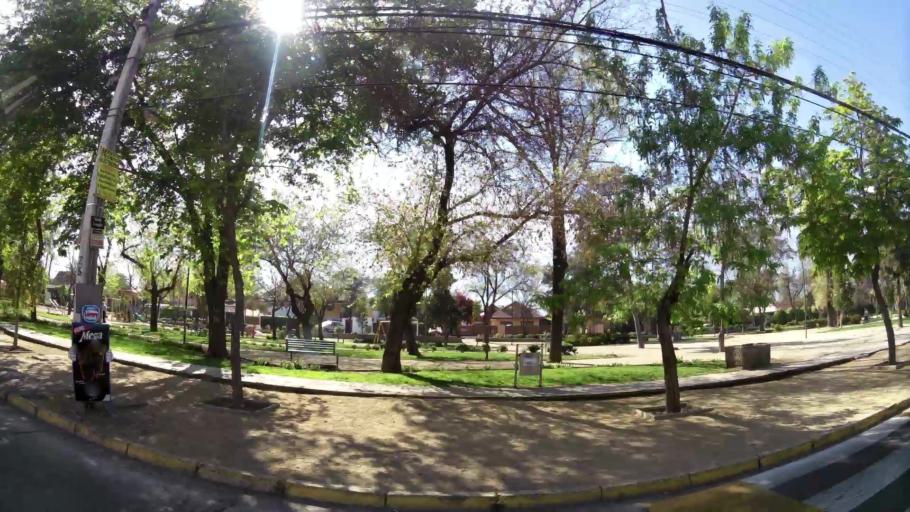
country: CL
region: Santiago Metropolitan
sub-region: Provincia de Santiago
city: Villa Presidente Frei, Nunoa, Santiago, Chile
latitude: -33.4489
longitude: -70.5560
